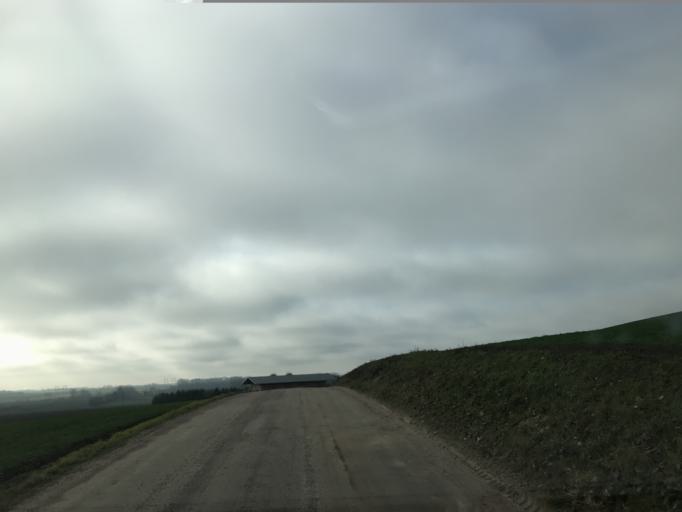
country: SE
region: Skane
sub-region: Svalovs Kommun
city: Teckomatorp
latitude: 55.8290
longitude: 13.0733
